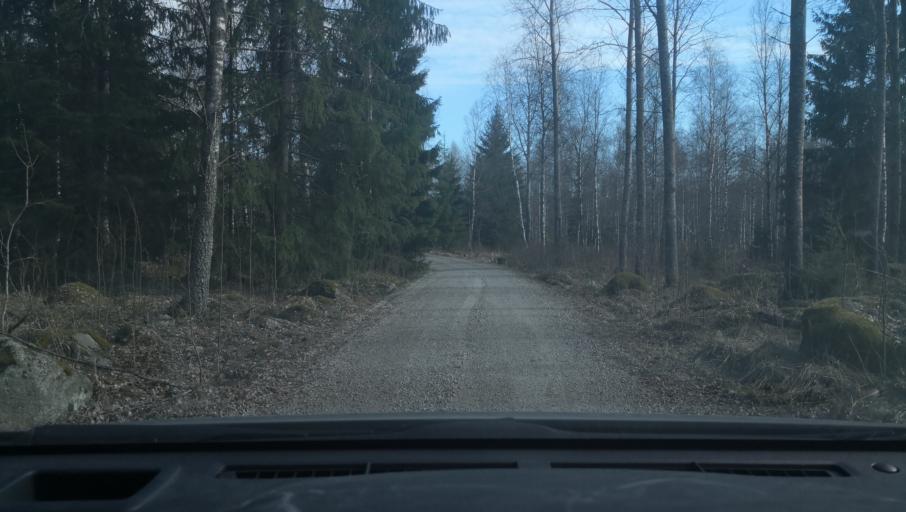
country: SE
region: Uppsala
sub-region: Heby Kommun
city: Heby
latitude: 59.8431
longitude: 16.8519
